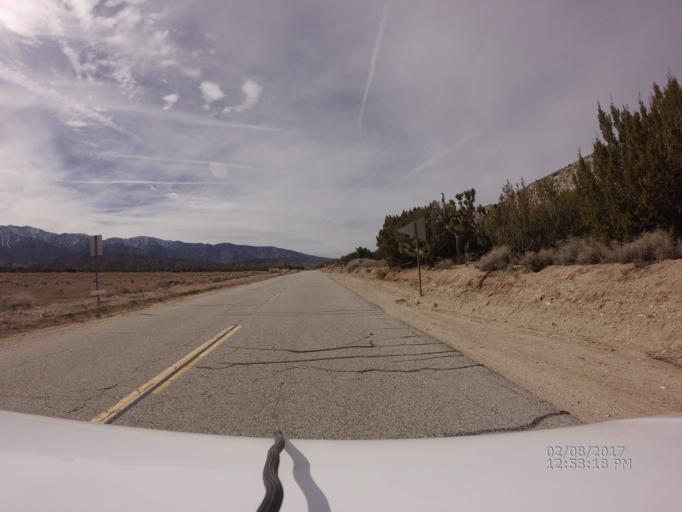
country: US
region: California
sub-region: Los Angeles County
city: Lake Los Angeles
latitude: 34.4500
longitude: -117.8205
